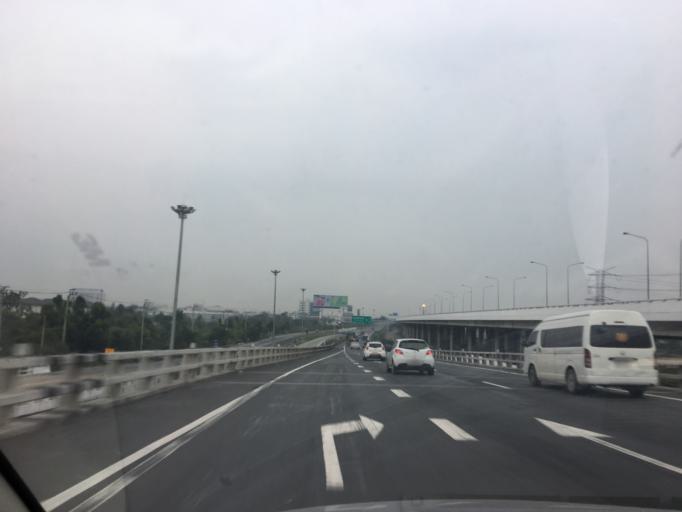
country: TH
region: Bangkok
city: Saphan Sung
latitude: 13.7306
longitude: 100.7030
